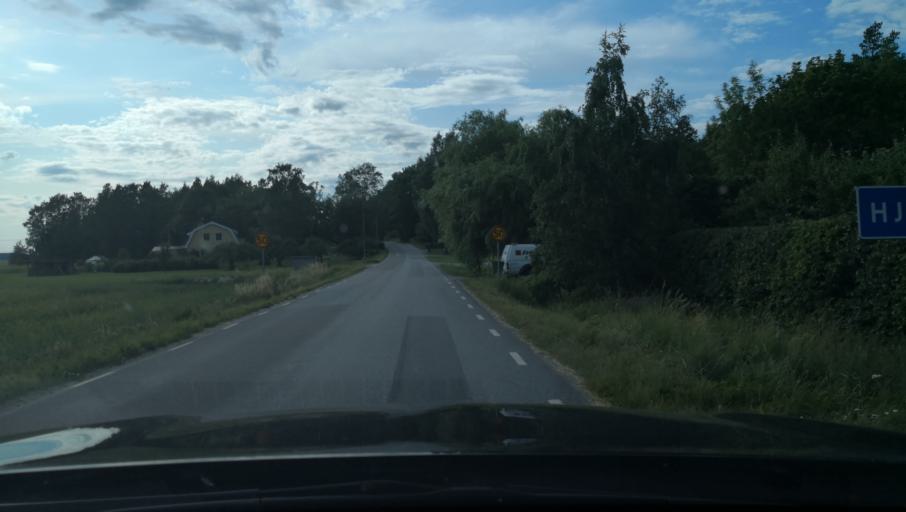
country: SE
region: Uppsala
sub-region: Enkopings Kommun
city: Orsundsbro
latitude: 59.6873
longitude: 17.3893
